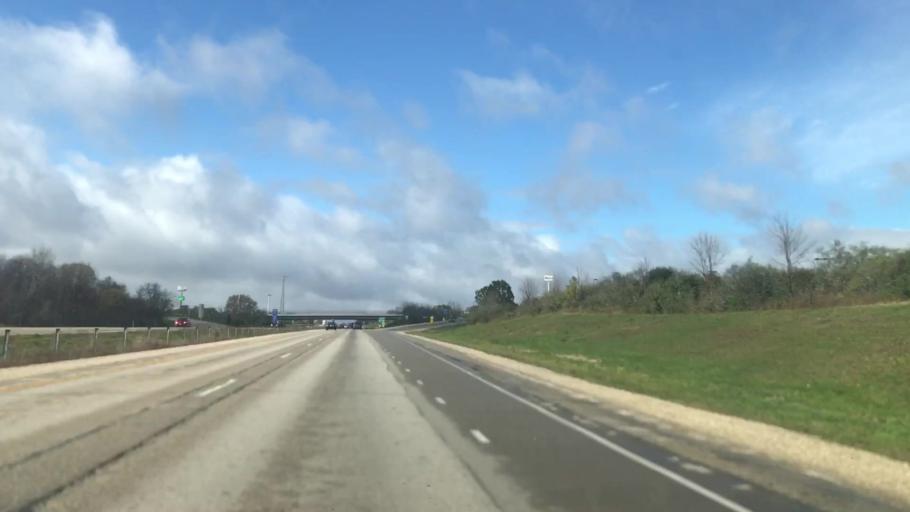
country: US
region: Wisconsin
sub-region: Washington County
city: Richfield
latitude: 43.2784
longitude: -88.1902
